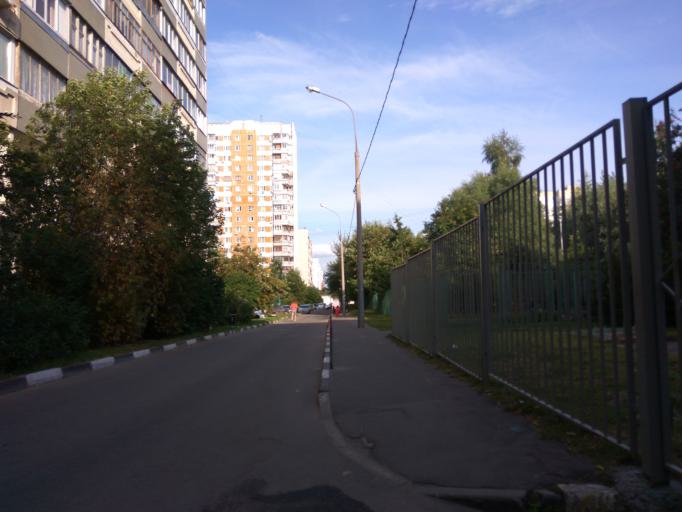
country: RU
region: Moscow
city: Chertanovo Yuzhnoye
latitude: 55.5707
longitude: 37.5715
